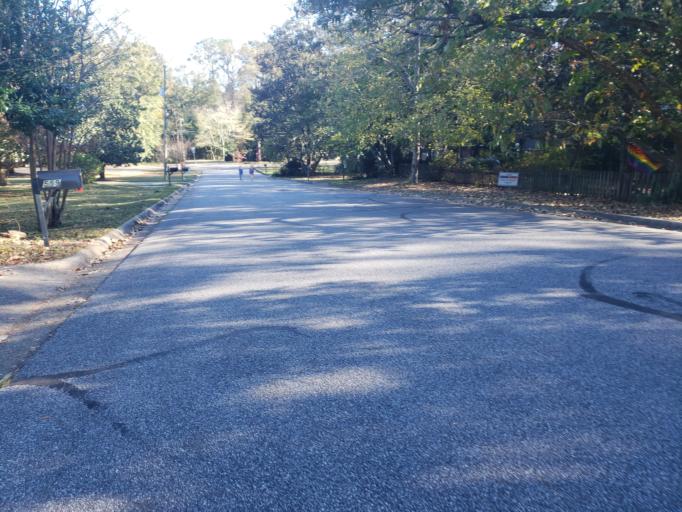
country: US
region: Alabama
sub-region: Lee County
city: Auburn
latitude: 32.5934
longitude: -85.4717
